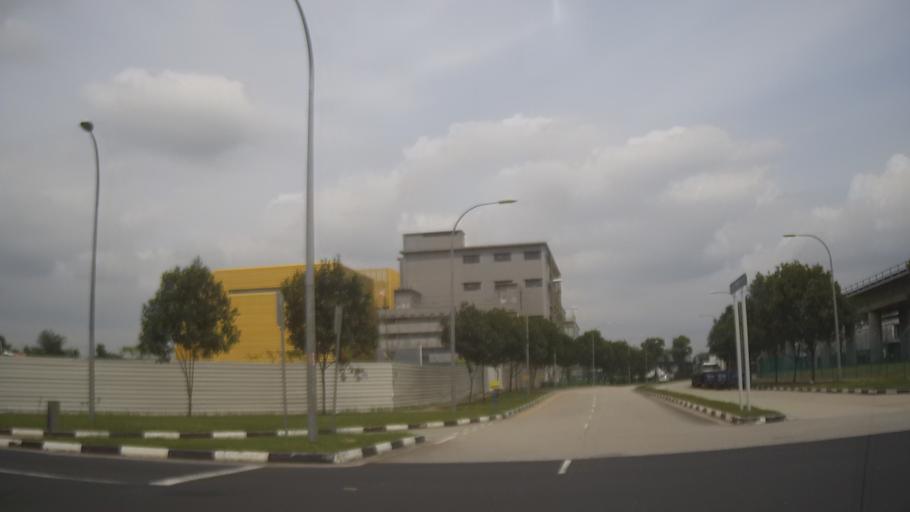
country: MY
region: Johor
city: Johor Bahru
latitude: 1.4142
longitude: 103.7483
